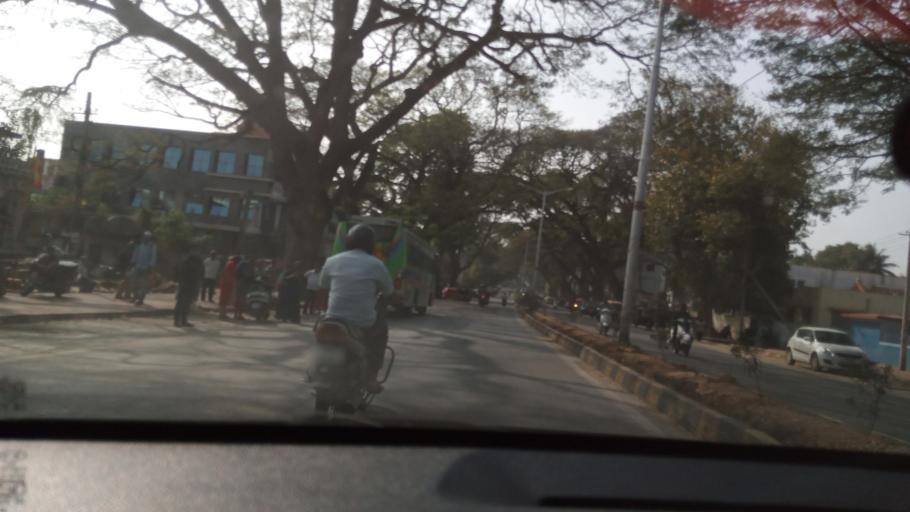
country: IN
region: Karnataka
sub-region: Mysore
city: Mysore
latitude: 12.3016
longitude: 76.6514
